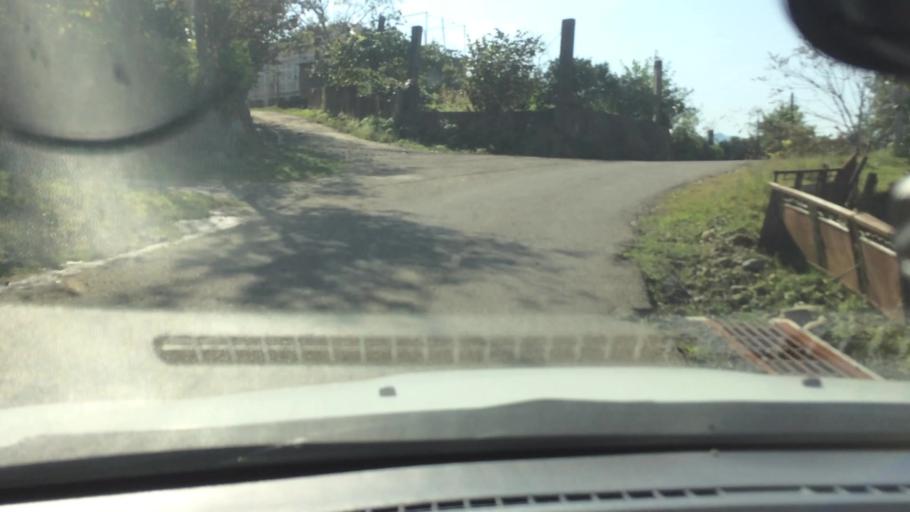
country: GE
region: Ajaria
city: Kobuleti
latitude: 41.8125
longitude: 41.8247
